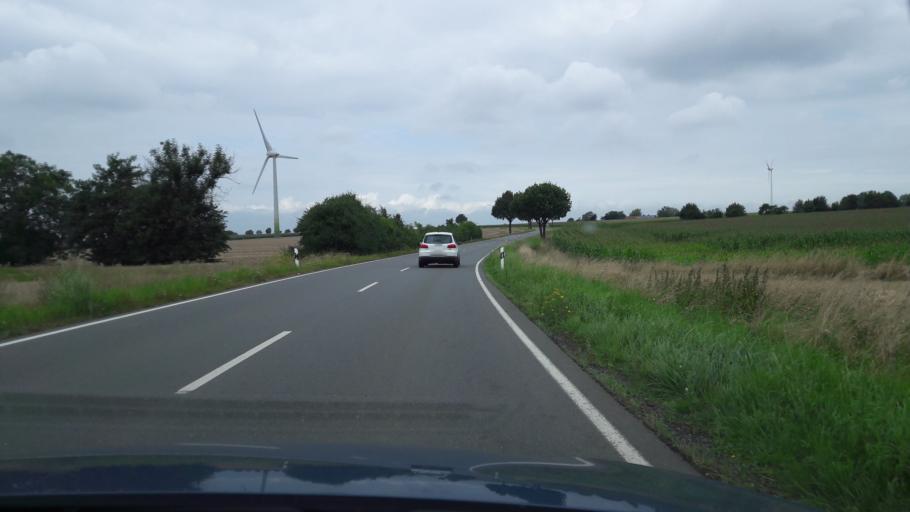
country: DE
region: North Rhine-Westphalia
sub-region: Regierungsbezirk Munster
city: Ennigerloh
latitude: 51.8591
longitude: 7.9766
